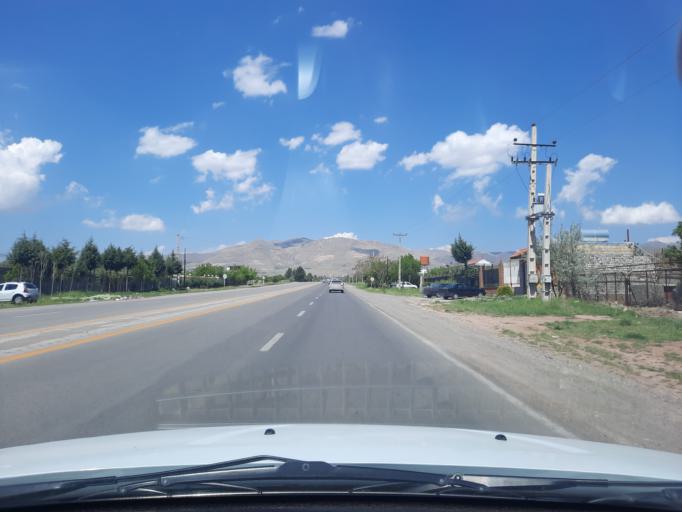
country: IR
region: Qazvin
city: Alvand
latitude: 36.3027
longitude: 50.1438
